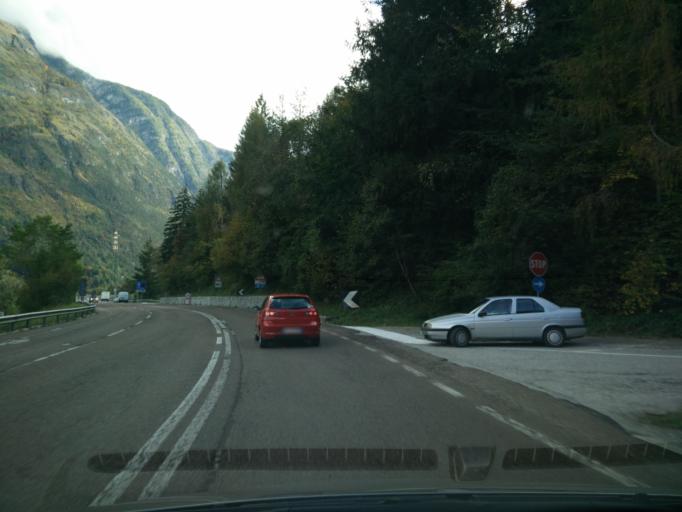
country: IT
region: Veneto
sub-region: Provincia di Belluno
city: Pieve di Cadore
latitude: 46.4088
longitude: 12.3670
